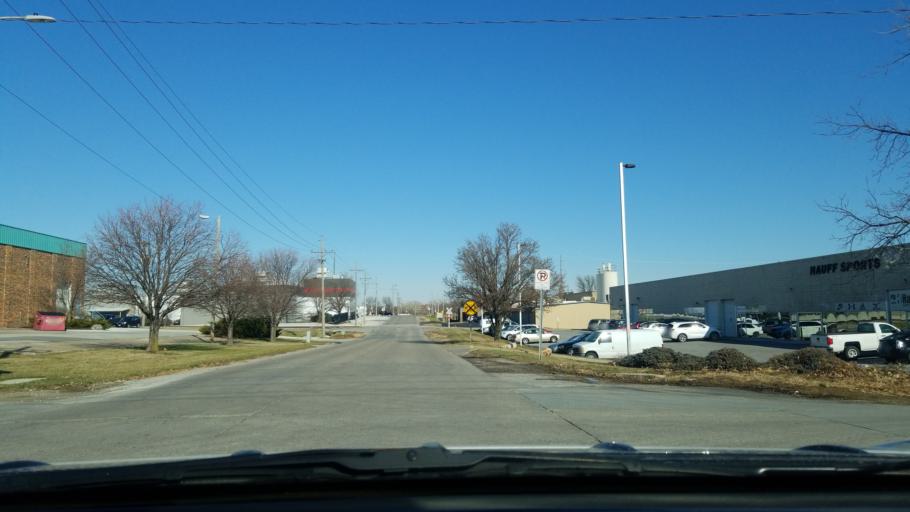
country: US
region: Nebraska
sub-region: Douglas County
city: Ralston
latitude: 41.2142
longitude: -96.0719
